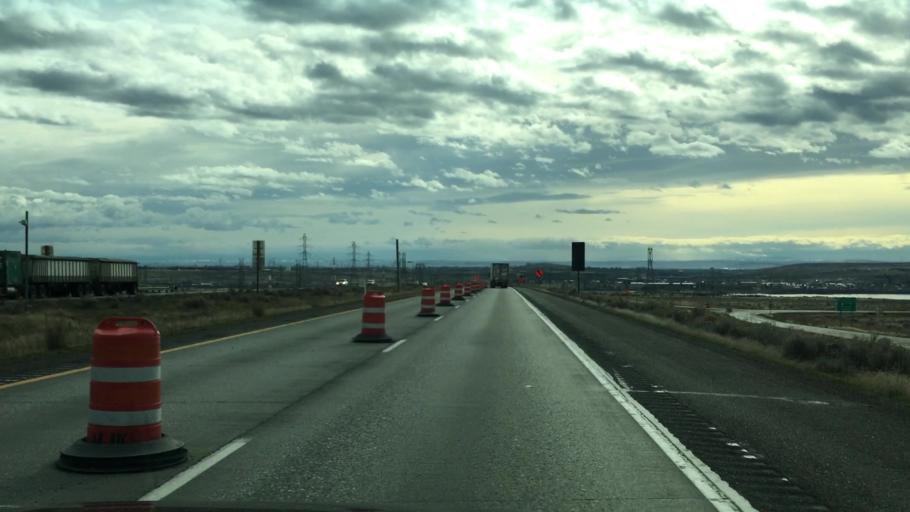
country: US
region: Oregon
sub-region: Umatilla County
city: Umatilla
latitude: 45.9477
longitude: -119.3365
